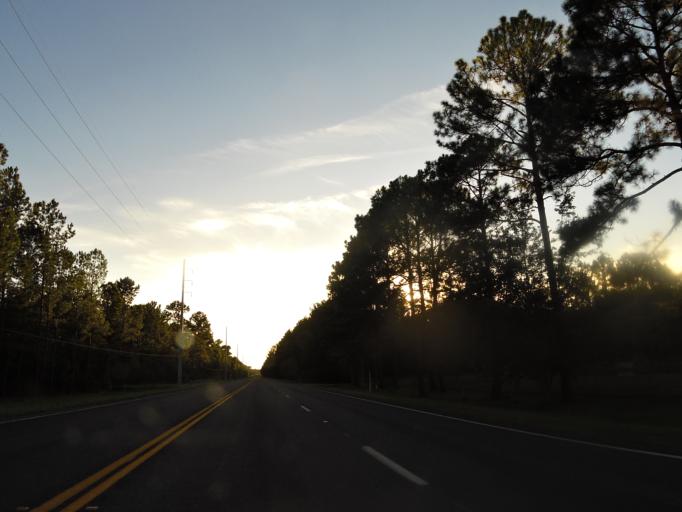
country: US
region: Georgia
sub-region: Camden County
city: Woodbine
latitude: 31.1028
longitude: -81.6945
